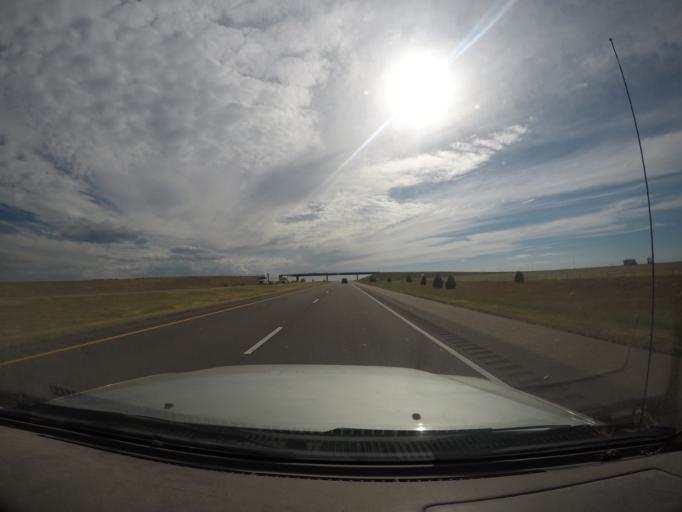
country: US
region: Nebraska
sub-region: Kimball County
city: Kimball
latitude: 41.2062
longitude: -103.7176
